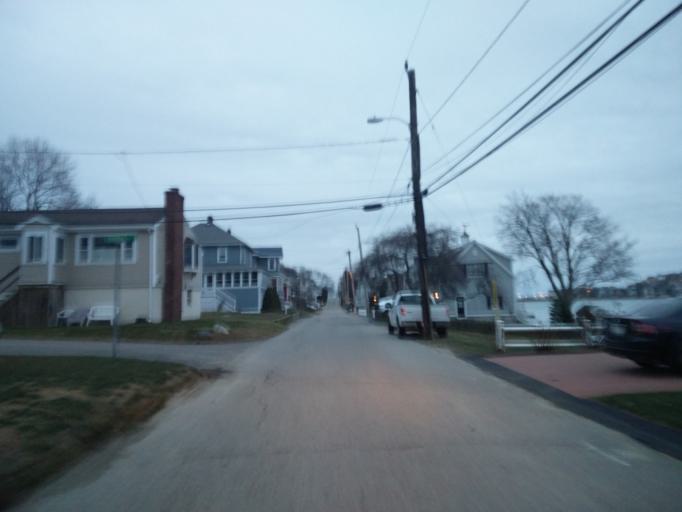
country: US
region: Massachusetts
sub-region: Plymouth County
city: Hingham
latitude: 42.2764
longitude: -70.8729
